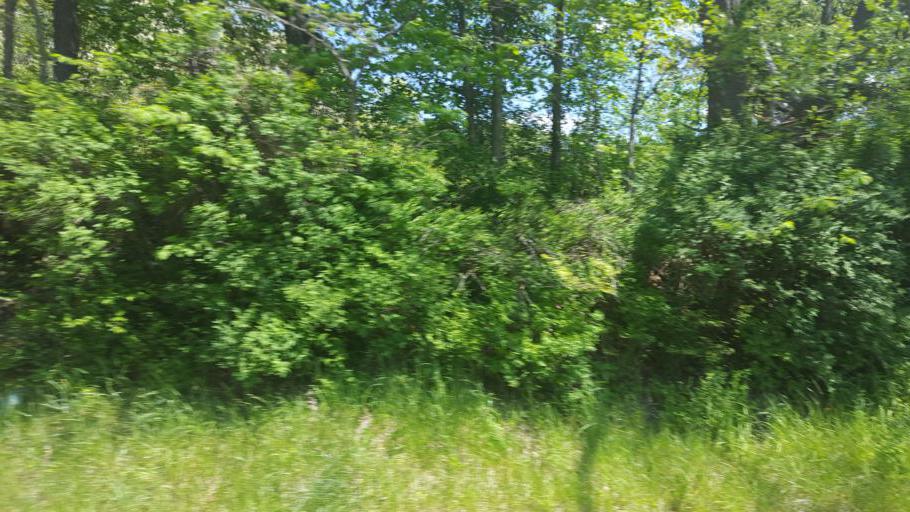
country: US
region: Ohio
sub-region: Knox County
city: Mount Vernon
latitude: 40.3599
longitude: -82.4521
